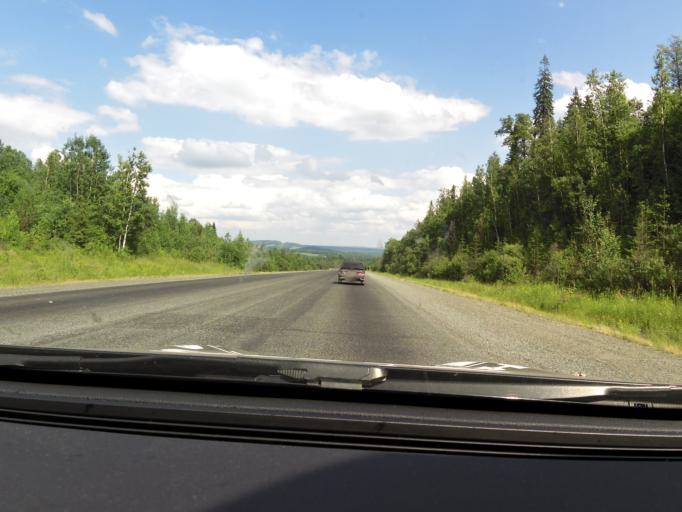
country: RU
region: Sverdlovsk
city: Arti
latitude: 56.7875
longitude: 58.5514
